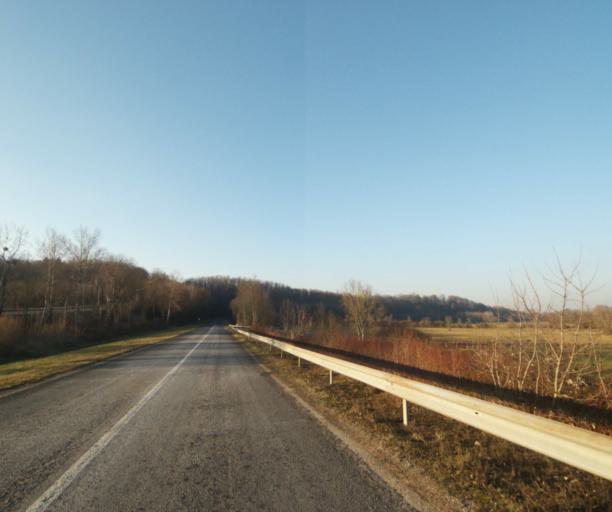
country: FR
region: Champagne-Ardenne
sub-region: Departement de la Haute-Marne
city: Bienville
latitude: 48.5679
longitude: 5.0412
